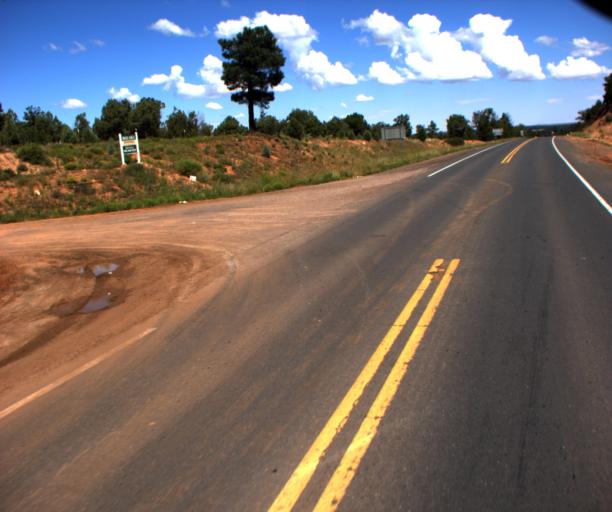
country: US
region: Arizona
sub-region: Navajo County
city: Show Low
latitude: 34.2685
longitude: -110.0928
